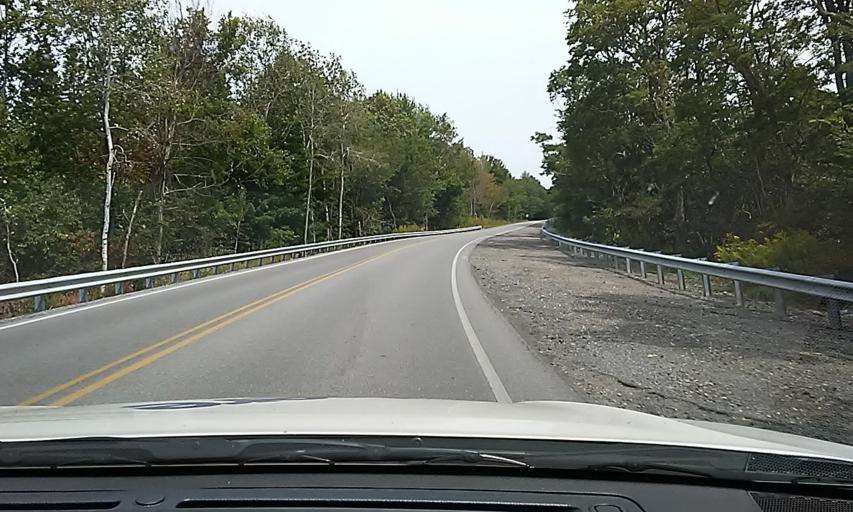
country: US
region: Pennsylvania
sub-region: Elk County
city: Saint Marys
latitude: 41.3368
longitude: -78.6285
